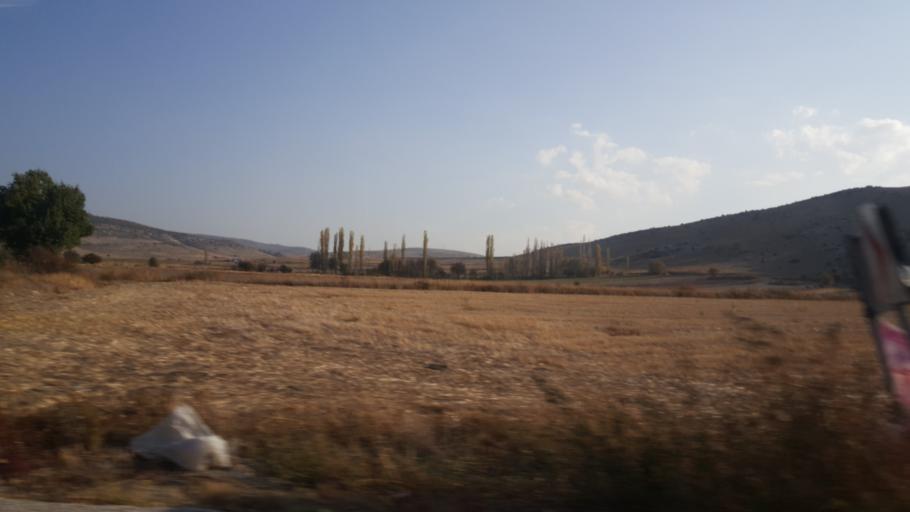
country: TR
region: Eskisehir
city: Seyitgazi
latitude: 39.4245
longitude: 30.6612
